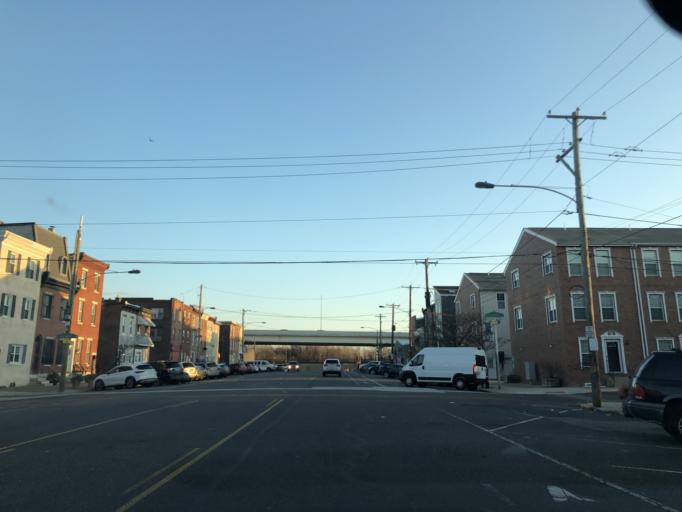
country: US
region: New Jersey
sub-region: Camden County
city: Camden
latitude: 39.9784
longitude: -75.1148
